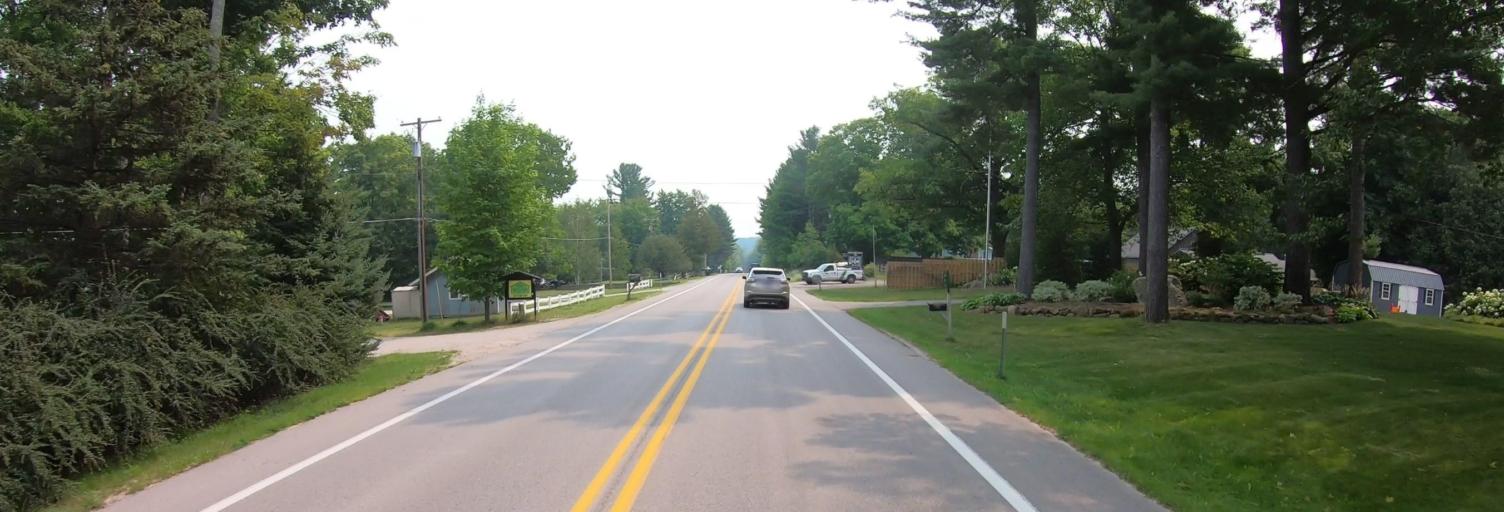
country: US
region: Michigan
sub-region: Leelanau County
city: Leland
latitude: 44.9161
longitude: -85.8435
